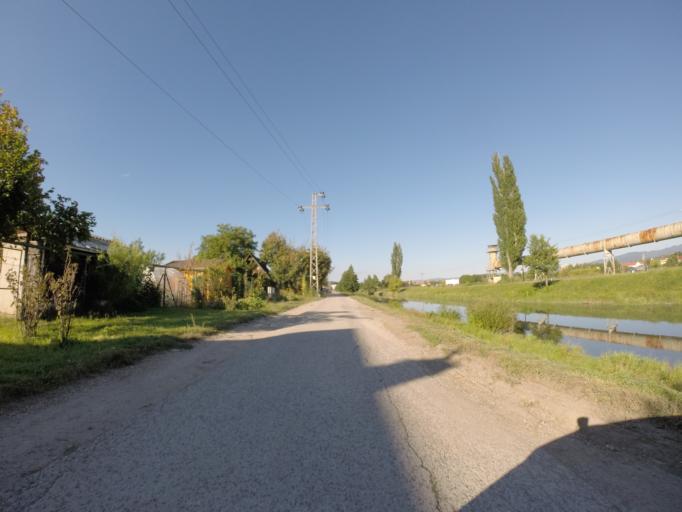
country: SK
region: Nitriansky
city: Novaky
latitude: 48.7149
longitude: 18.5282
